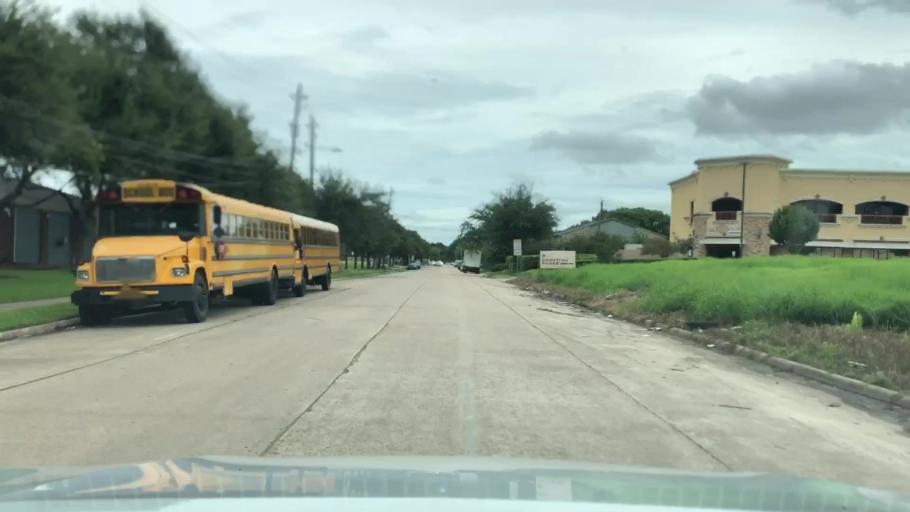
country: US
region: Texas
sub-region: Fort Bend County
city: Meadows Place
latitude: 29.7006
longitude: -95.5558
